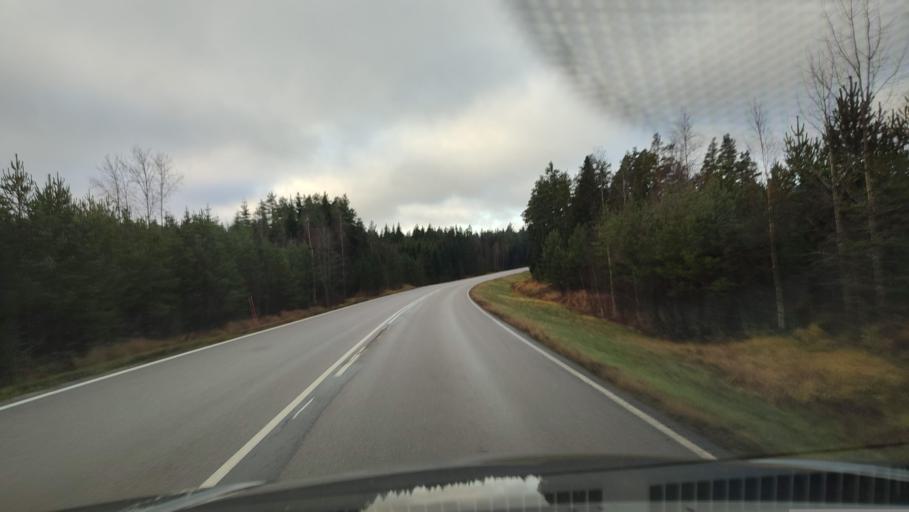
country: FI
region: Ostrobothnia
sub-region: Sydosterbotten
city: Kristinestad
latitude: 62.3053
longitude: 21.4406
